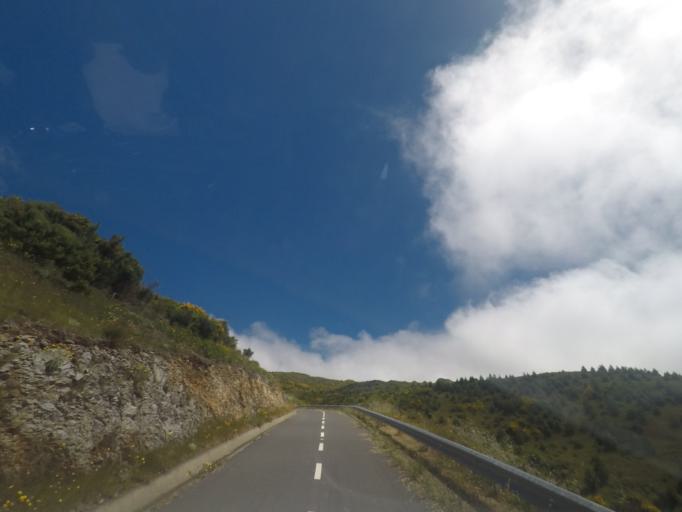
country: PT
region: Madeira
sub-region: Camara de Lobos
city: Curral das Freiras
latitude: 32.7089
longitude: -16.9395
